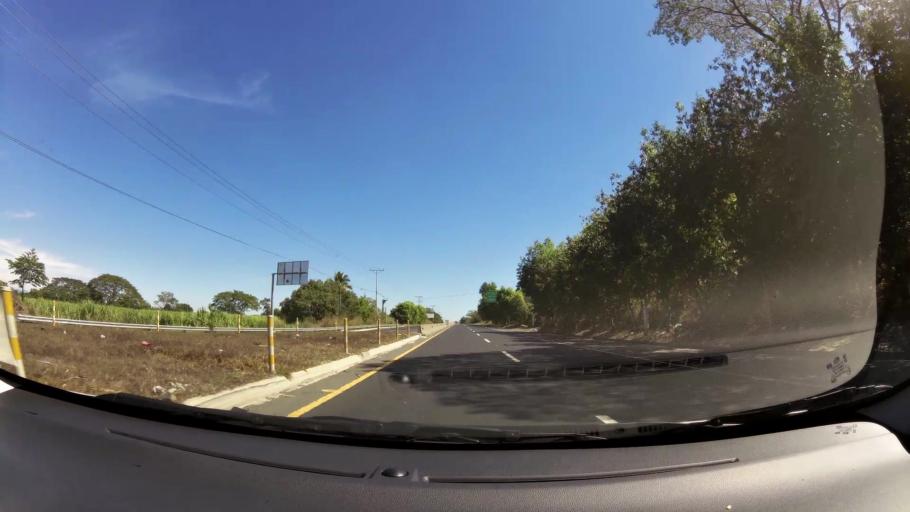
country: SV
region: La Libertad
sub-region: Distrito de Quezaltepeque
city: Quezaltepeque
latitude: 13.8190
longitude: -89.2977
